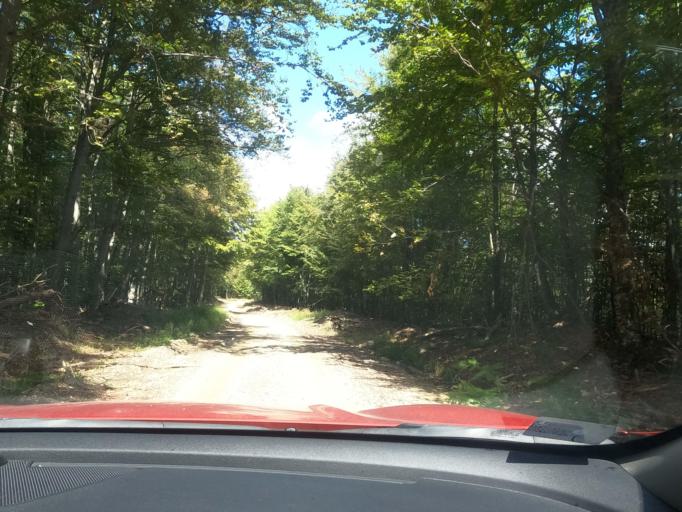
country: BA
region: Federation of Bosnia and Herzegovina
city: Velika Kladusa
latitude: 45.2711
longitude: 15.7778
